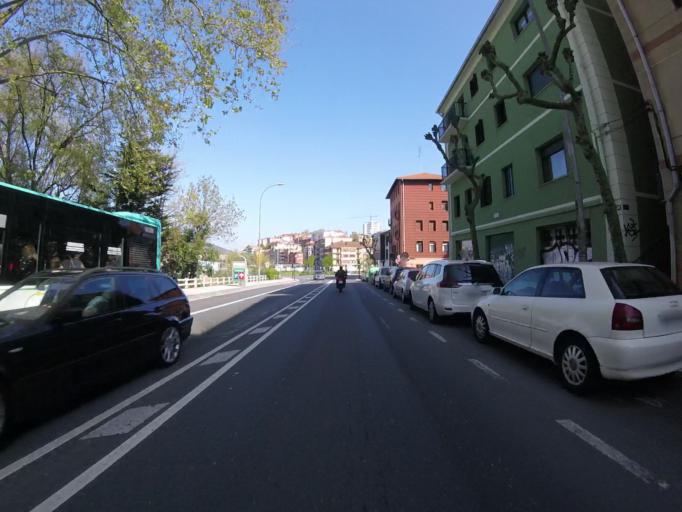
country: ES
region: Basque Country
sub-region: Provincia de Guipuzcoa
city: Pasaia
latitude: 43.3198
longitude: -1.9400
